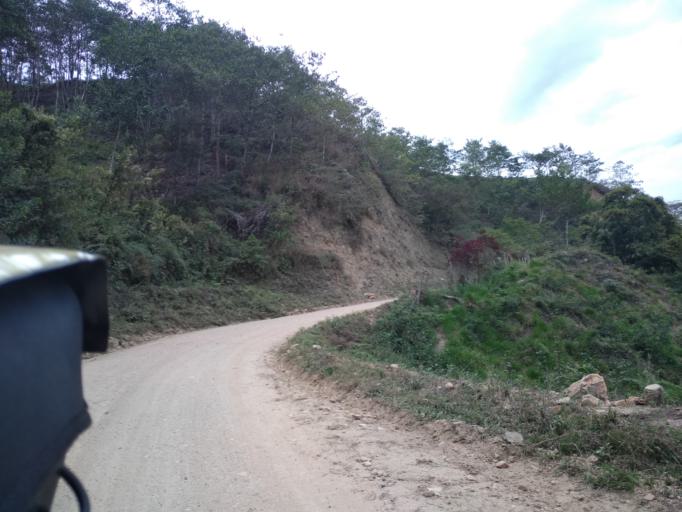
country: PE
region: Cajamarca
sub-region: Provincia de San Ignacio
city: Namballe
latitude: -4.9344
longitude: -79.1026
